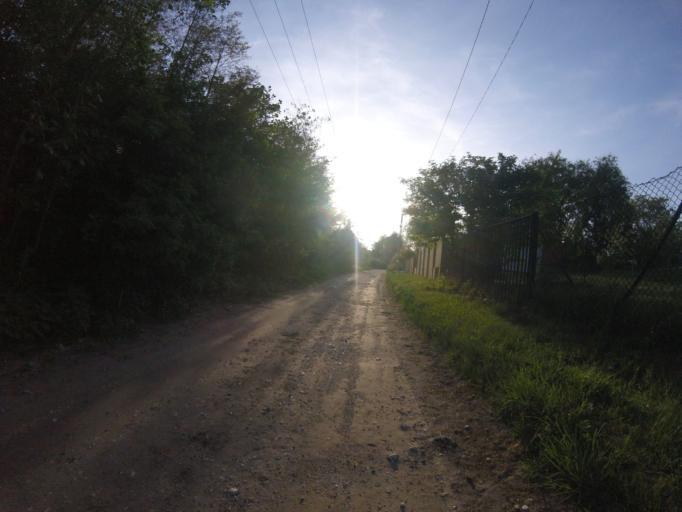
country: HU
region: Pest
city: Pilisszentivan
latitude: 47.6134
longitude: 18.8782
